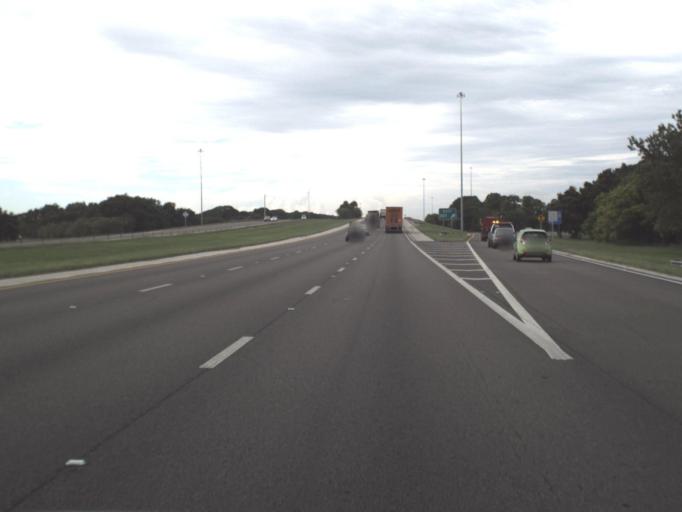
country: US
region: Florida
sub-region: Sarasota County
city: Lake Sarasota
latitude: 27.3035
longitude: -82.4483
